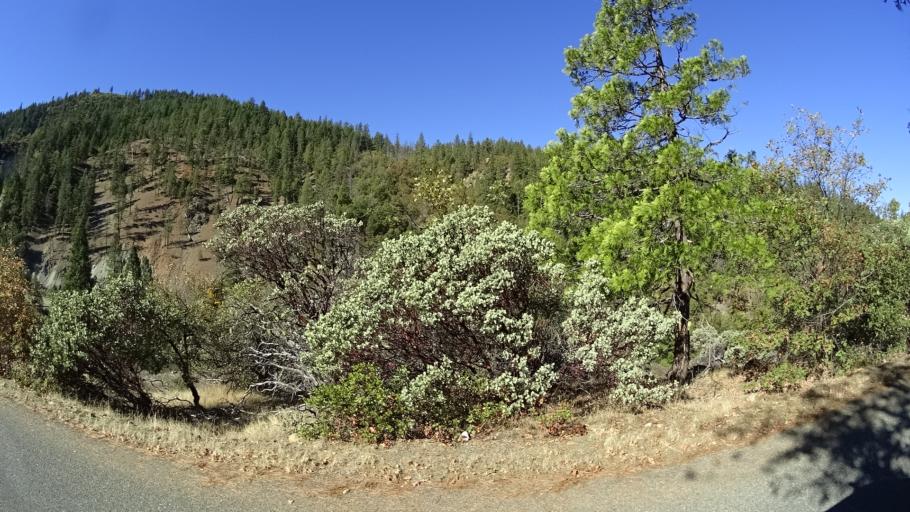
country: US
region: California
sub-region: Humboldt County
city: Willow Creek
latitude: 41.1893
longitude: -123.2164
